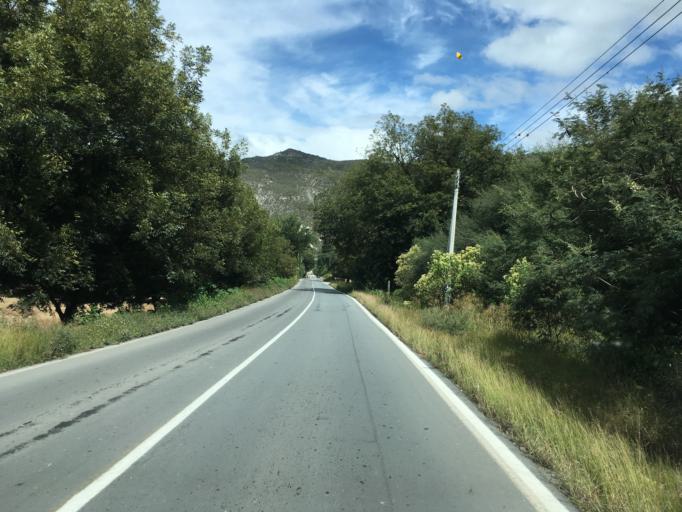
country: MX
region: Hidalgo
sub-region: San Agustin Metzquititlan
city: Mezquititlan
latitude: 20.4943
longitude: -98.6958
